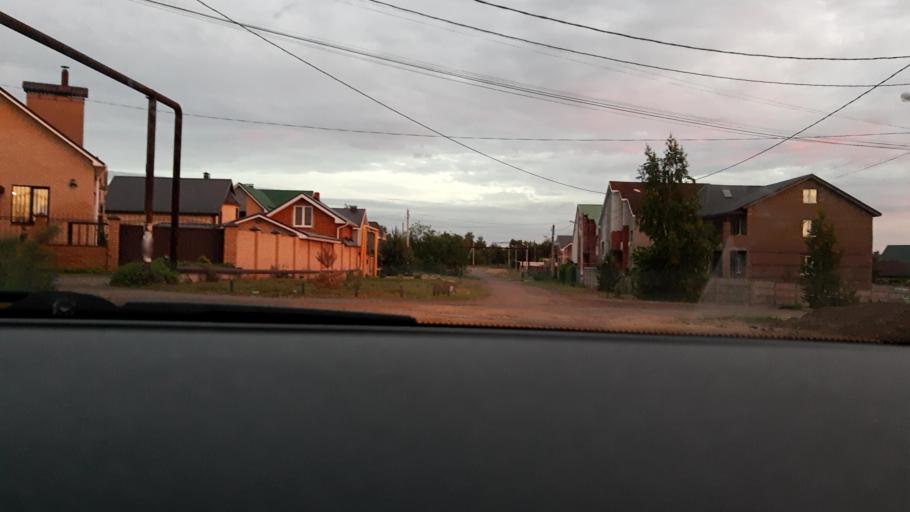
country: RU
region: Nizjnij Novgorod
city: Gorbatovka
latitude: 56.3848
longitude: 43.7663
